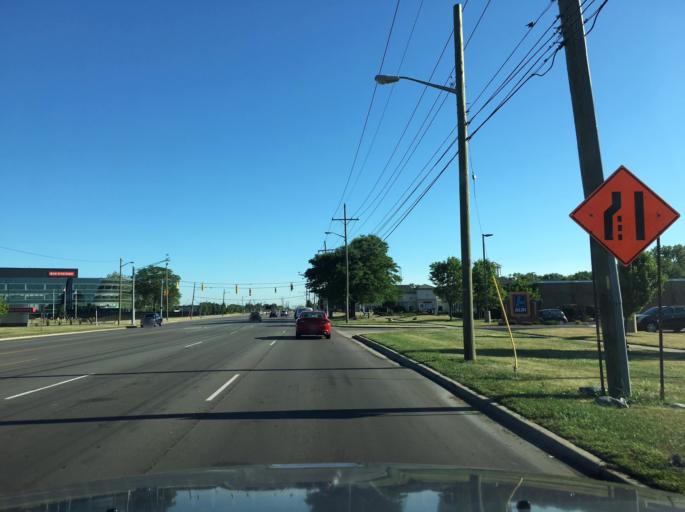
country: US
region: Michigan
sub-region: Macomb County
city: Sterling Heights
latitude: 42.5441
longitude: -83.0286
